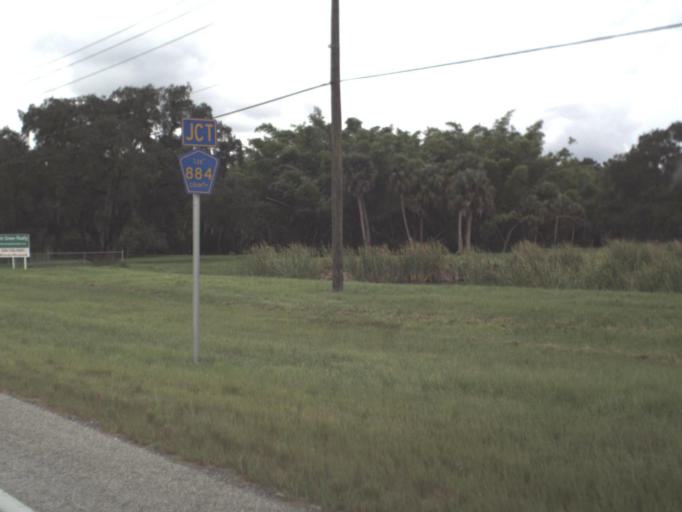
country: US
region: Florida
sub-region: Lee County
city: Alva
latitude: 26.7092
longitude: -81.5979
